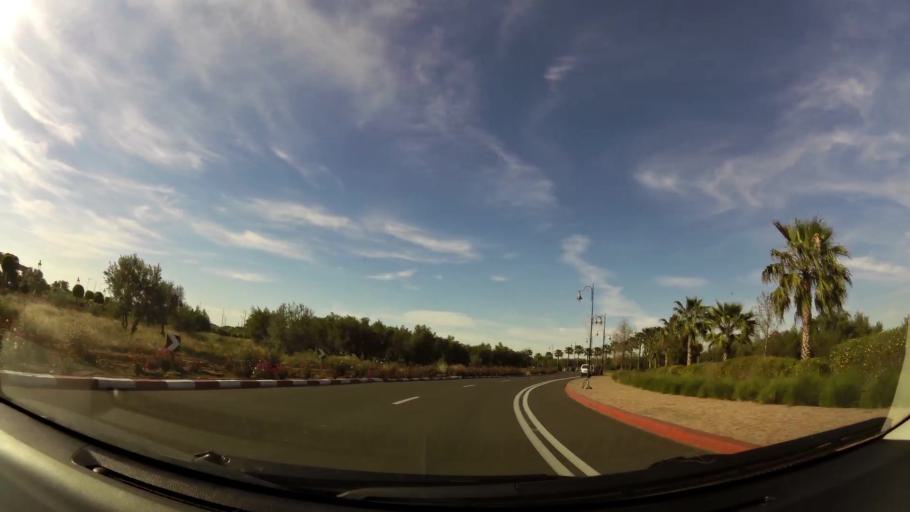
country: MA
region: Marrakech-Tensift-Al Haouz
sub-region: Marrakech
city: Marrakesh
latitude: 31.6129
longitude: -8.0041
